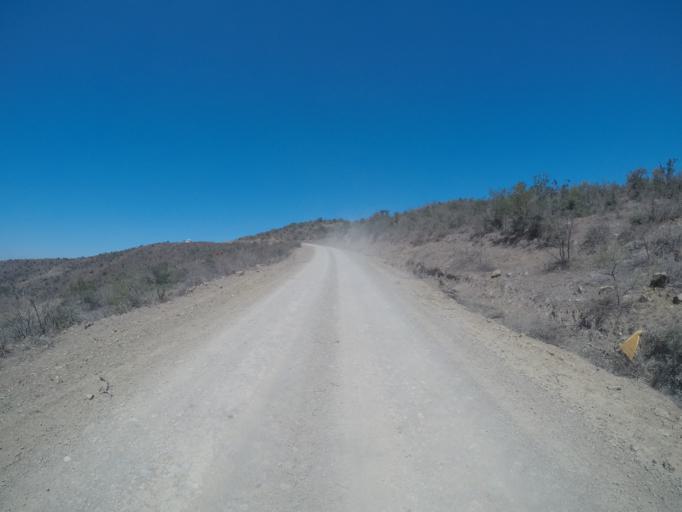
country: ZA
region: Eastern Cape
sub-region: OR Tambo District Municipality
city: Mthatha
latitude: -31.8762
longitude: 28.8731
